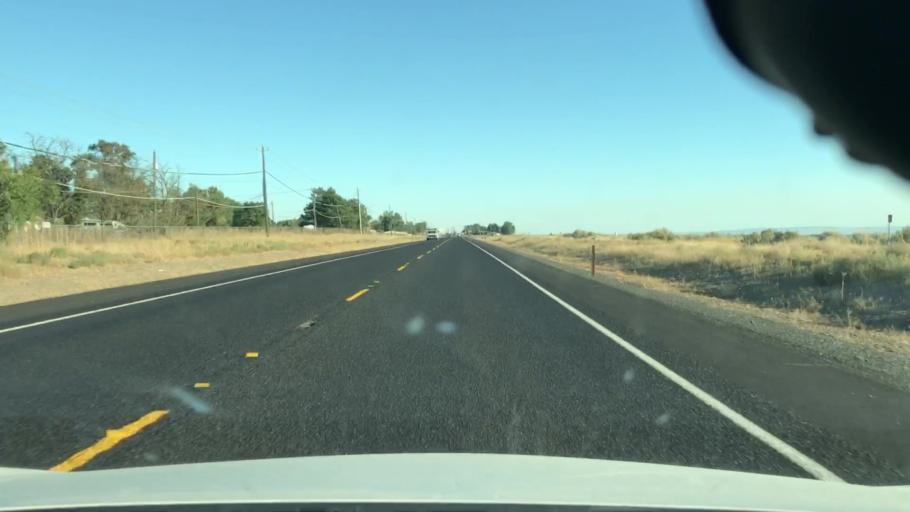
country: US
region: Washington
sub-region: Grant County
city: Moses Lake North
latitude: 47.1711
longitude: -119.3289
